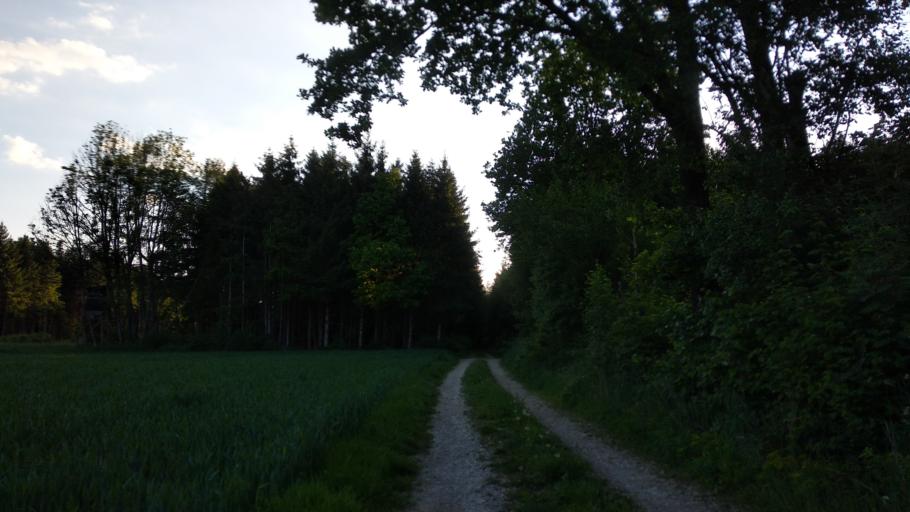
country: DE
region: Bavaria
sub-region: Upper Bavaria
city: Zorneding
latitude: 48.0827
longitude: 11.8021
